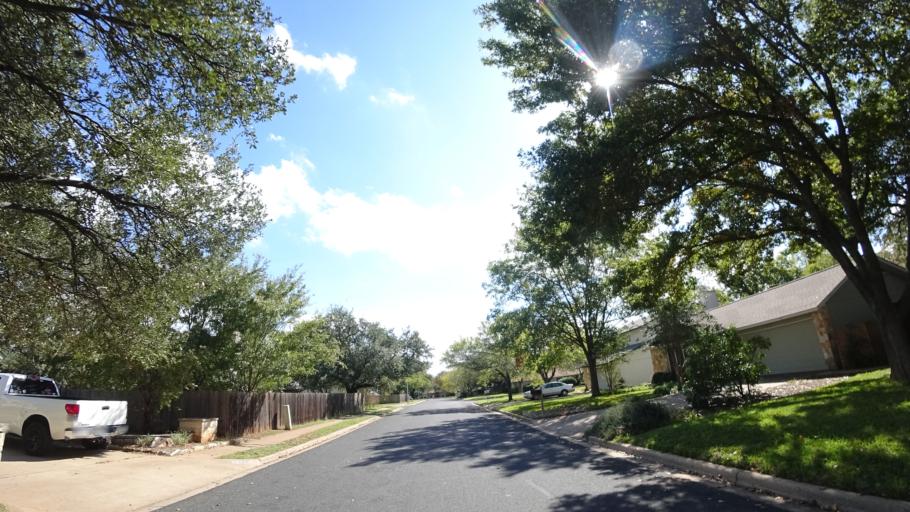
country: US
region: Texas
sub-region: Travis County
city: Wells Branch
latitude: 30.4158
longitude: -97.7228
